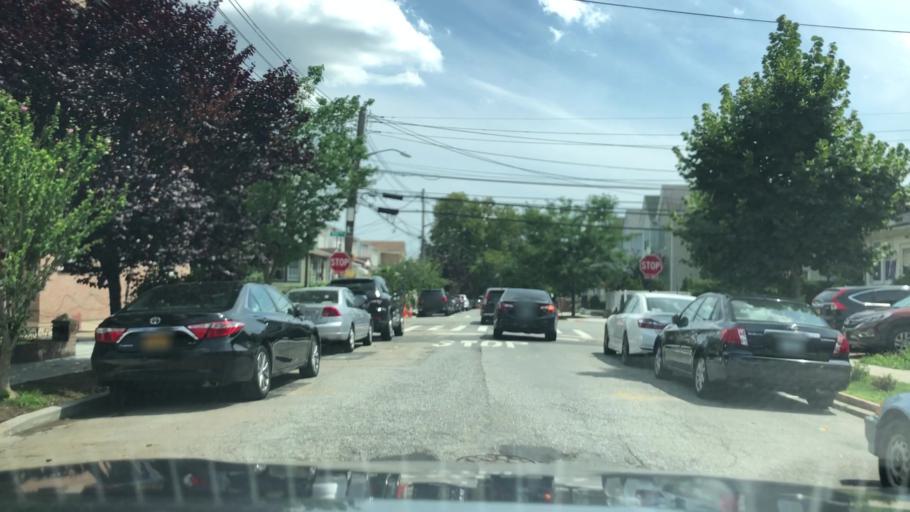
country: US
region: New York
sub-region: Queens County
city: Jamaica
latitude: 40.7113
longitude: -73.7819
